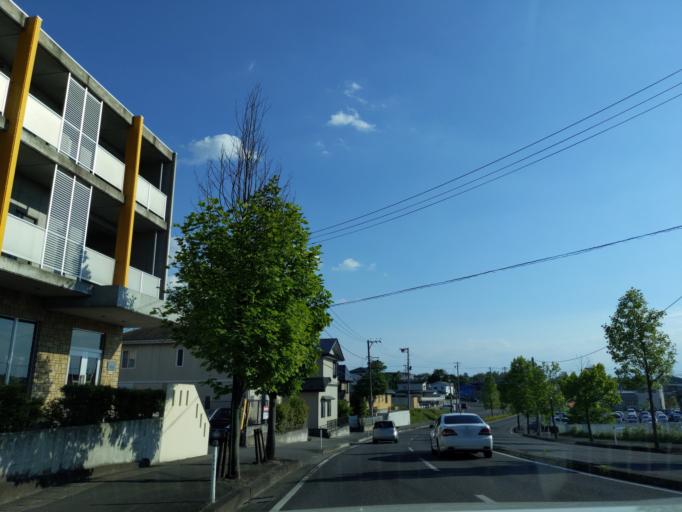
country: JP
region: Fukushima
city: Sukagawa
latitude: 37.2832
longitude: 140.3852
